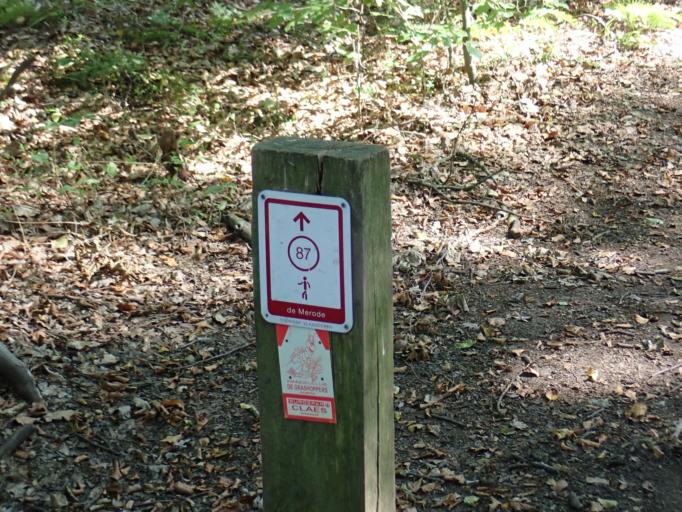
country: BE
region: Flanders
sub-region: Provincie Vlaams-Brabant
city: Scherpenheuvel-Zichem
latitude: 51.0341
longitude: 4.9890
